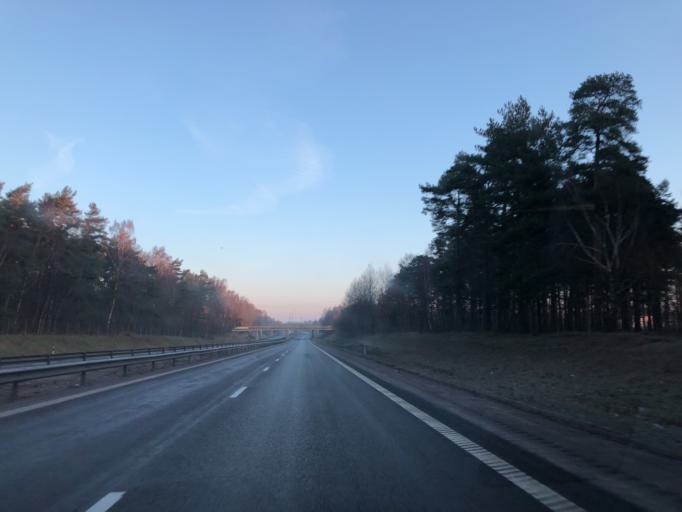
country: SE
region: Halland
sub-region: Halmstads Kommun
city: Halmstad
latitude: 56.6837
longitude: 12.8953
